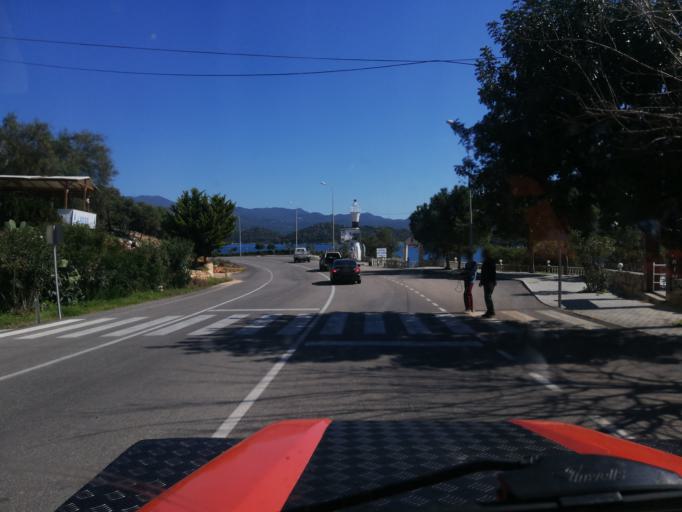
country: TR
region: Antalya
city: Kas
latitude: 36.2080
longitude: 29.6149
